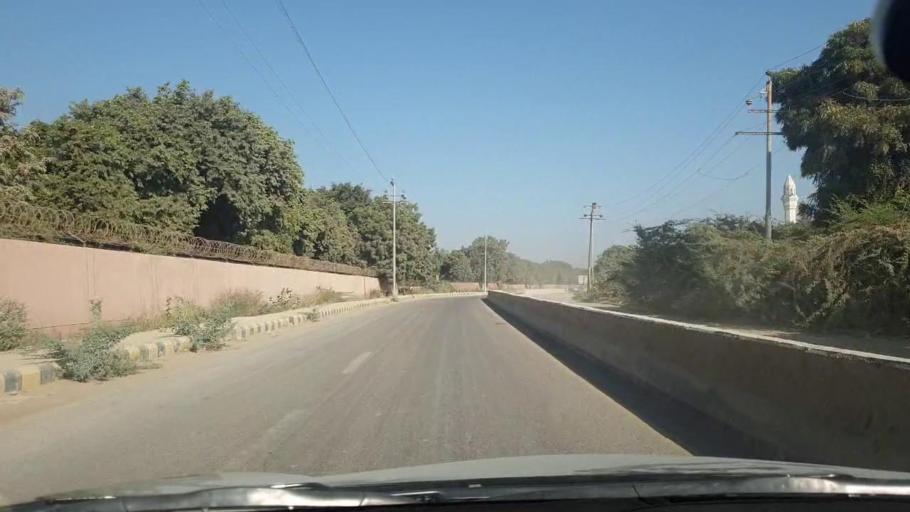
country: PK
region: Sindh
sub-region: Karachi District
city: Karachi
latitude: 25.0857
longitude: 67.0124
